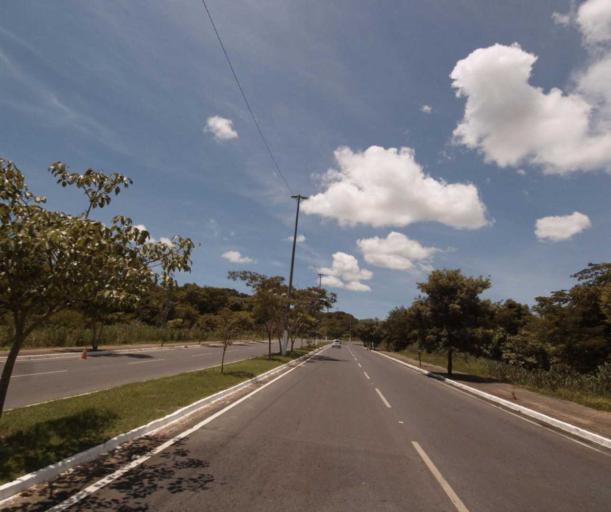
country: BR
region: Mato Grosso
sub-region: Cuiaba
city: Cuiaba
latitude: -15.5738
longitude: -56.1077
